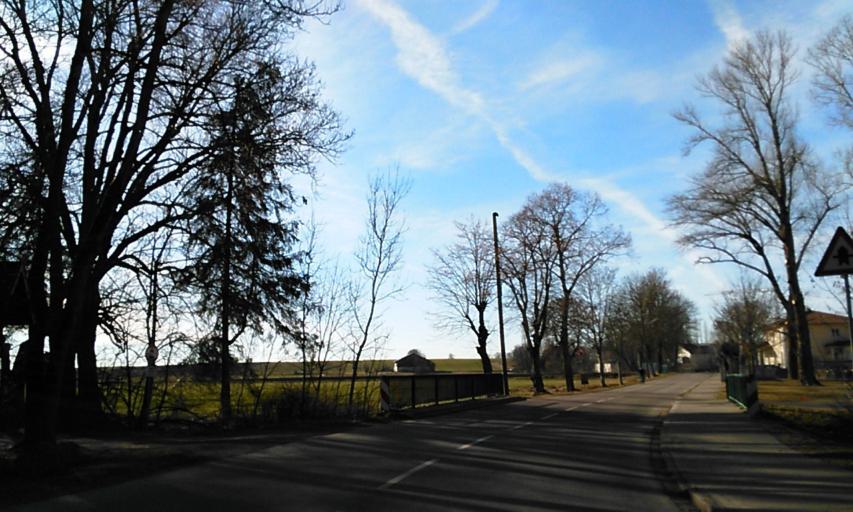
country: DE
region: Bavaria
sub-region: Swabia
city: Merching
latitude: 48.2449
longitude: 10.9813
